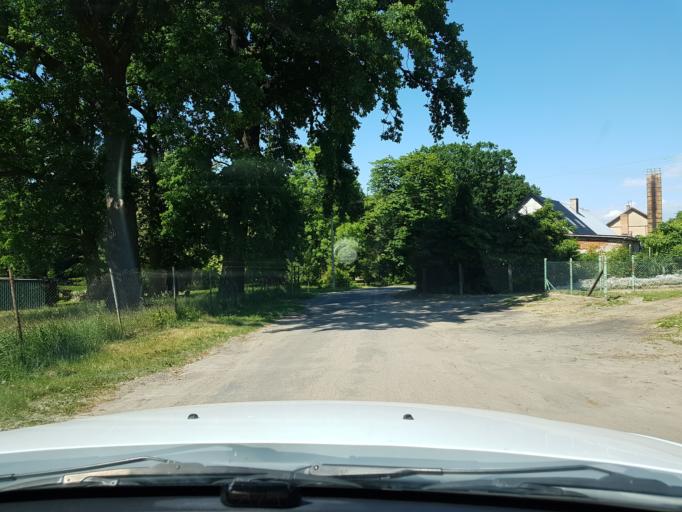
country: PL
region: West Pomeranian Voivodeship
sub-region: Powiat gryfinski
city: Banie
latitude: 53.1348
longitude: 14.5466
